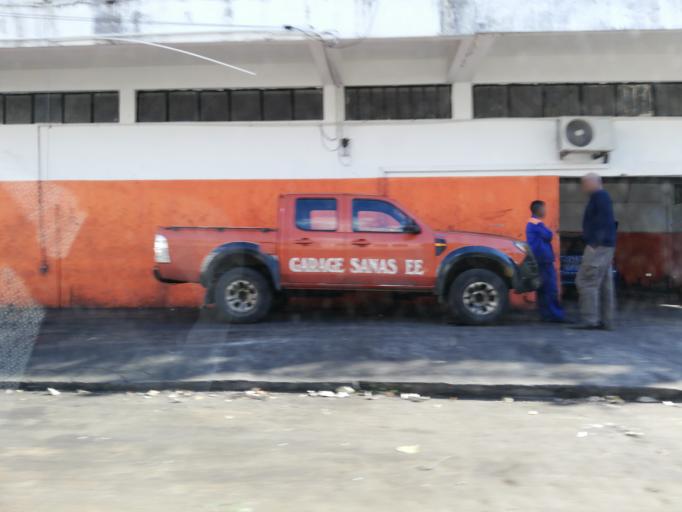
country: MU
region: Port Louis
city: Port Louis
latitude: -20.1615
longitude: 57.4901
